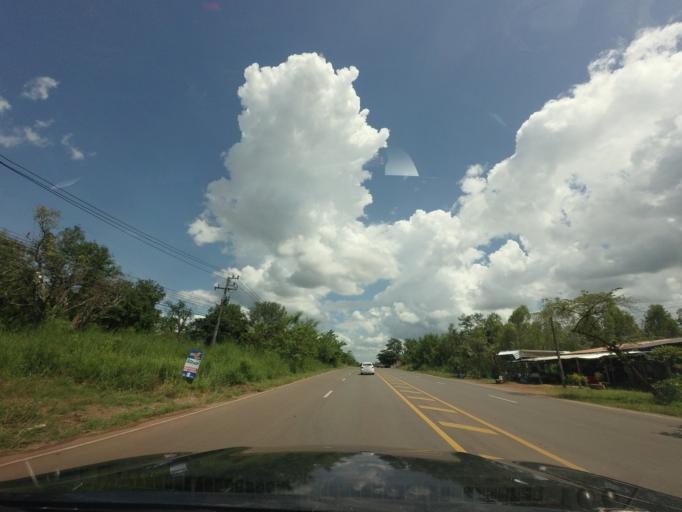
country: TH
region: Changwat Udon Thani
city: Ban Dung
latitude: 17.6844
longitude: 103.2115
